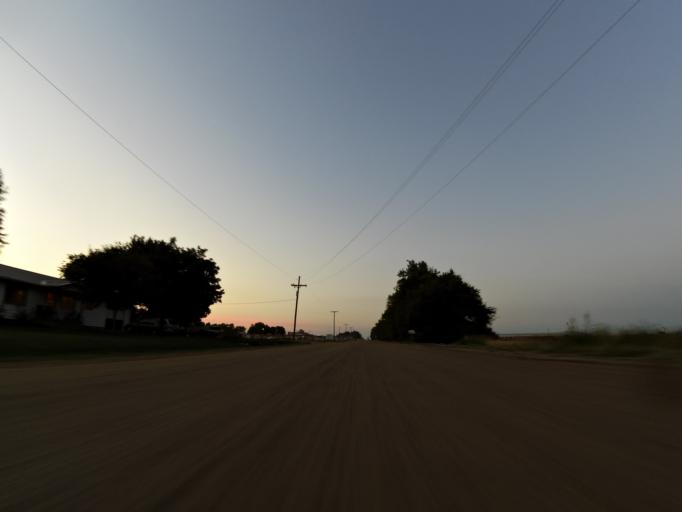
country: US
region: Kansas
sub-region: Reno County
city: South Hutchinson
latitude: 37.9916
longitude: -98.0319
